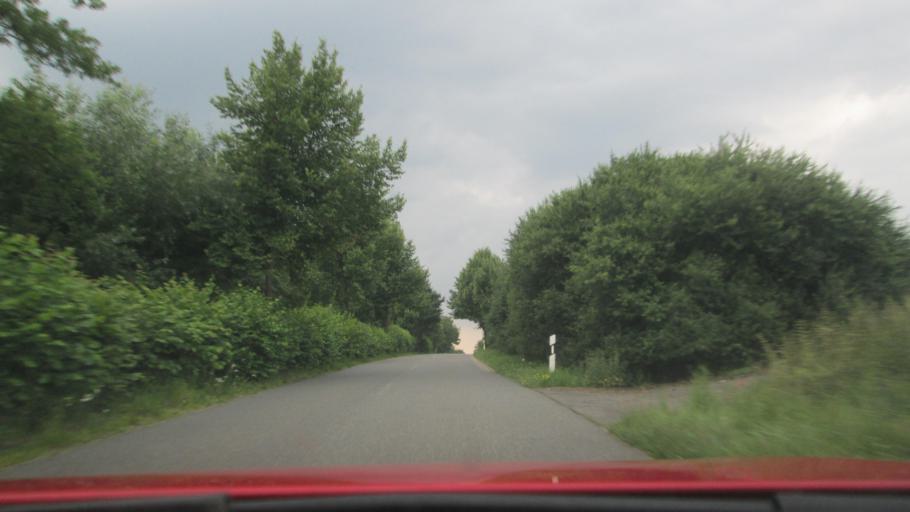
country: DE
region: Lower Saxony
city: Lehre
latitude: 52.3575
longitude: 10.7141
